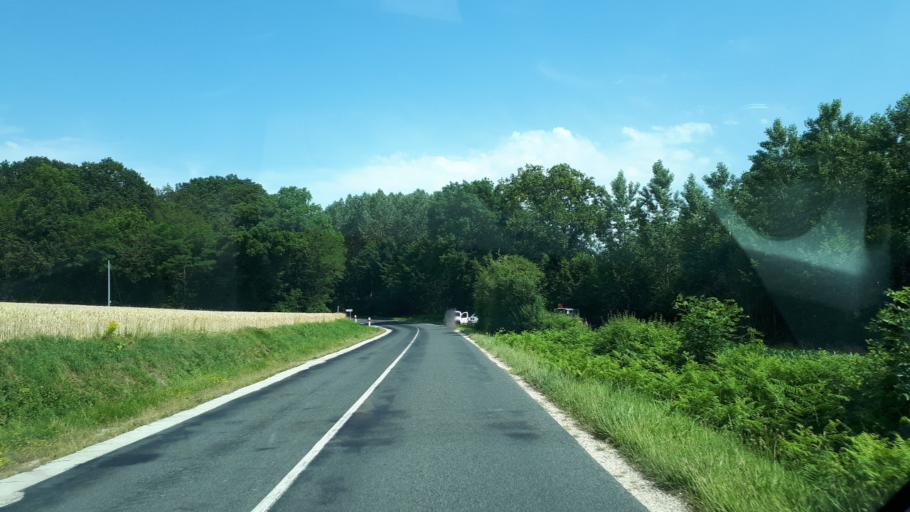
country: FR
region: Centre
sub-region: Departement du Loir-et-Cher
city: La Ville-aux-Clercs
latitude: 47.9309
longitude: 1.0853
